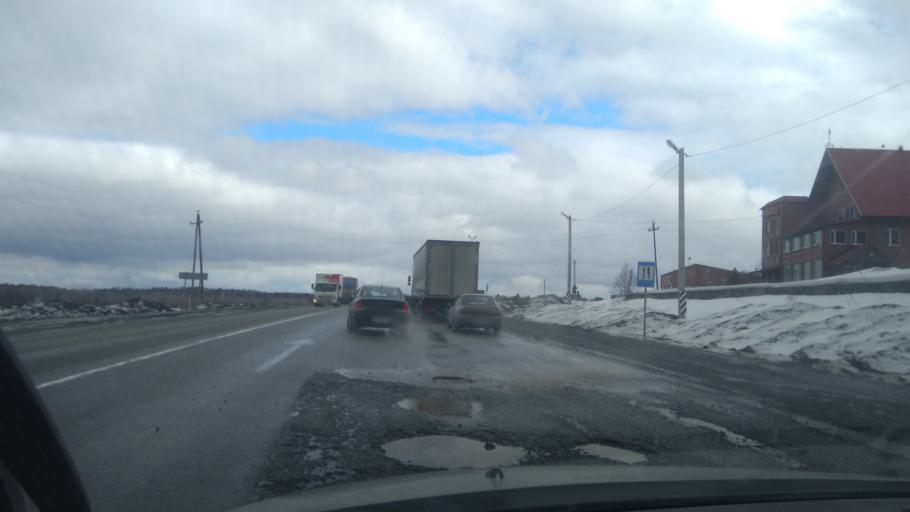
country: RU
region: Sverdlovsk
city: Bisert'
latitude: 56.8333
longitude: 58.7961
